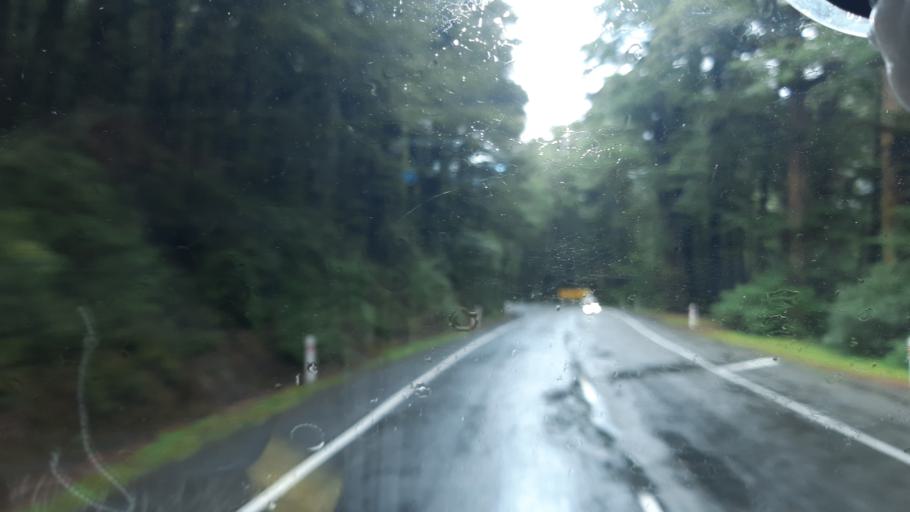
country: NZ
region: Canterbury
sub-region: Hurunui District
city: Amberley
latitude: -42.3775
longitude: 172.3500
